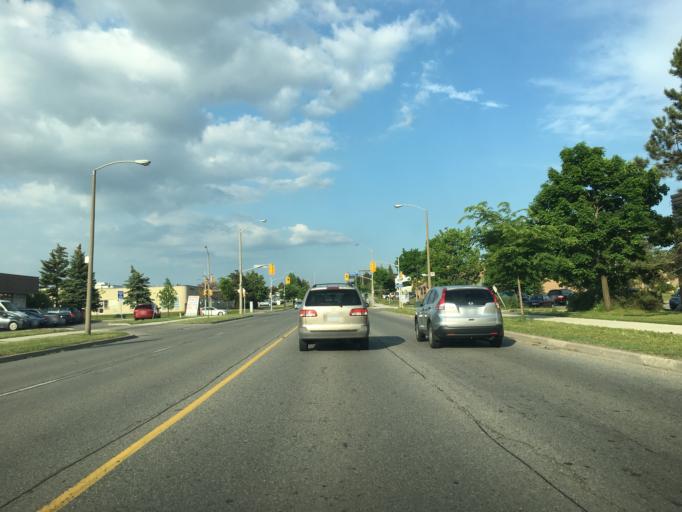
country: CA
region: Ontario
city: Markham
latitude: 43.8231
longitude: -79.2525
